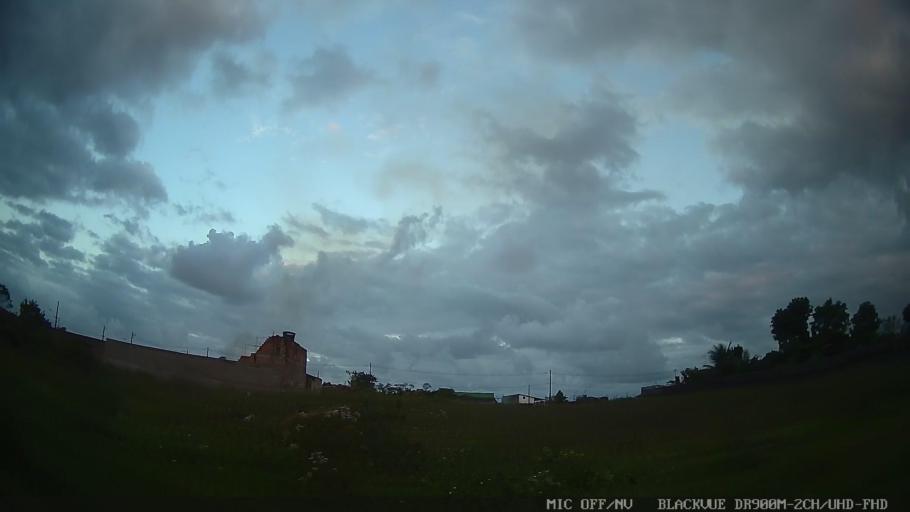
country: BR
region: Sao Paulo
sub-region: Itanhaem
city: Itanhaem
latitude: -24.1840
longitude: -46.8359
